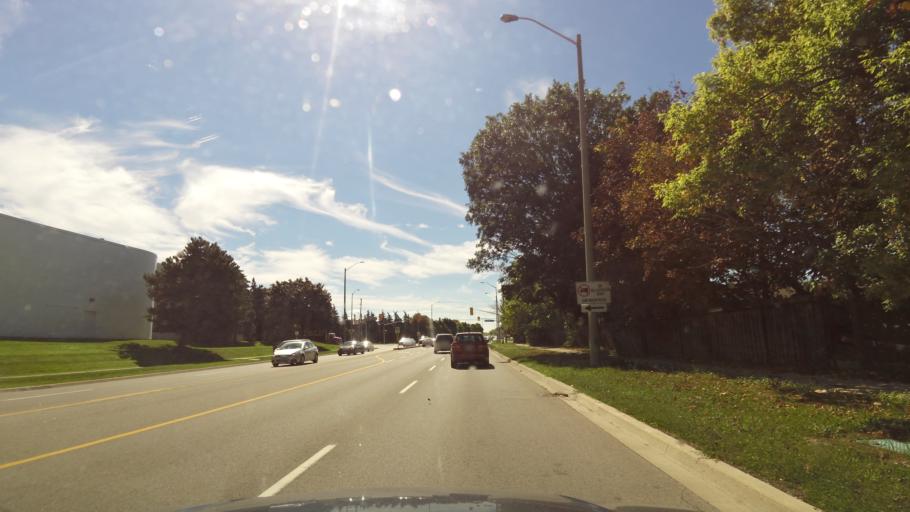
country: CA
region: Ontario
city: Mississauga
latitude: 43.6136
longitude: -79.6839
